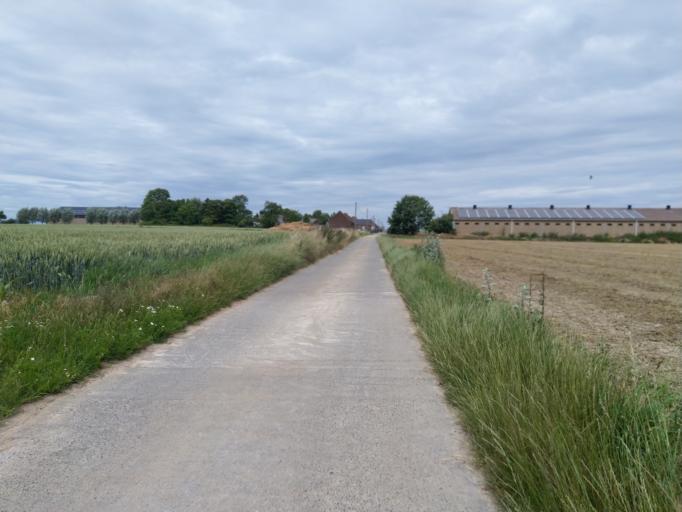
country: BE
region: Wallonia
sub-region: Province du Hainaut
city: Chievres
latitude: 50.5444
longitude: 3.7851
